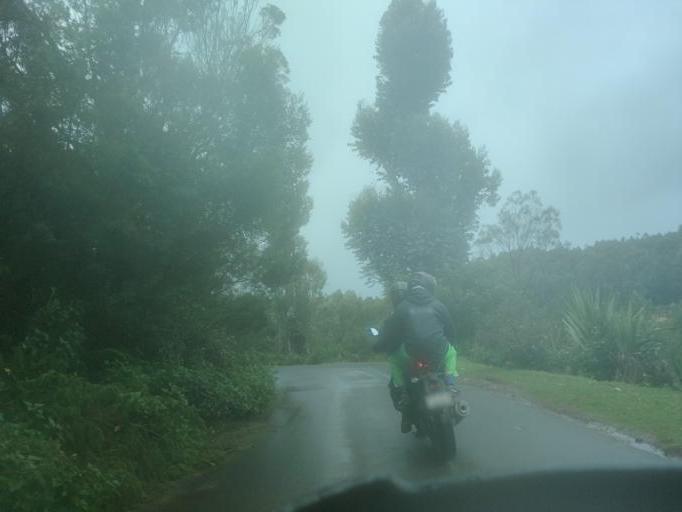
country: IN
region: Tamil Nadu
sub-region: Dindigul
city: Kodaikanal
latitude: 10.2218
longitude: 77.3551
